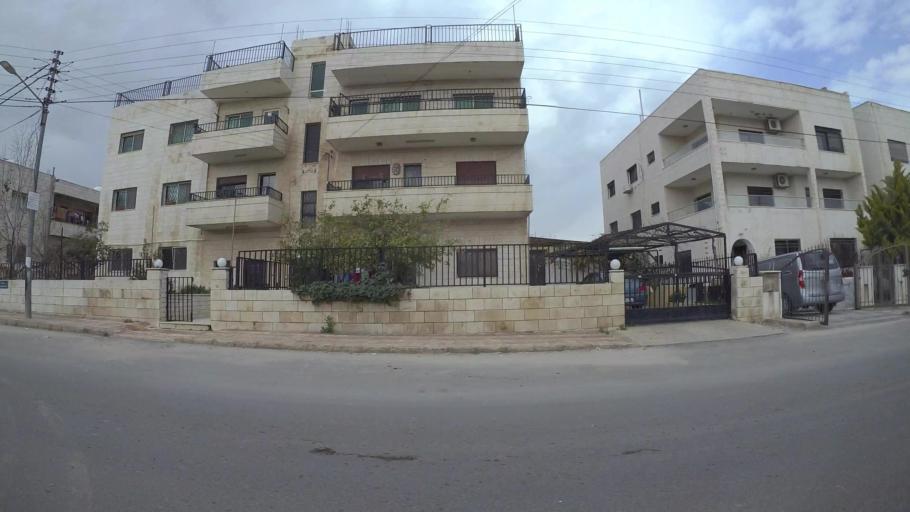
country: JO
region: Amman
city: Umm as Summaq
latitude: 31.8925
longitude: 35.8446
